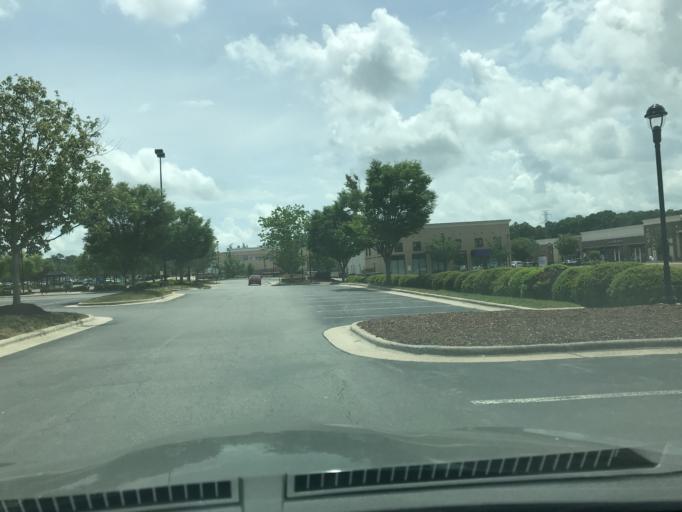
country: US
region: North Carolina
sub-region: Wake County
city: Raleigh
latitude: 35.8661
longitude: -78.5696
